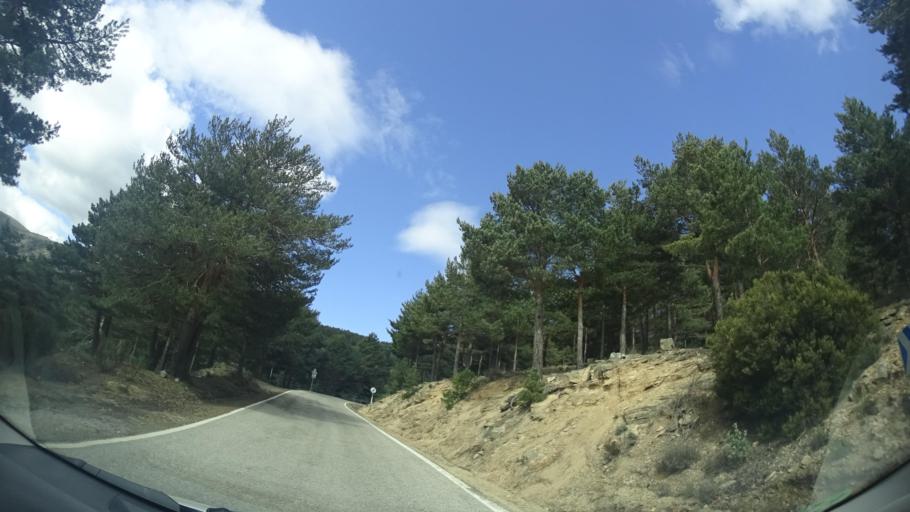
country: ES
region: Madrid
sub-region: Provincia de Madrid
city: Canencia
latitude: 40.8664
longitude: -3.7599
